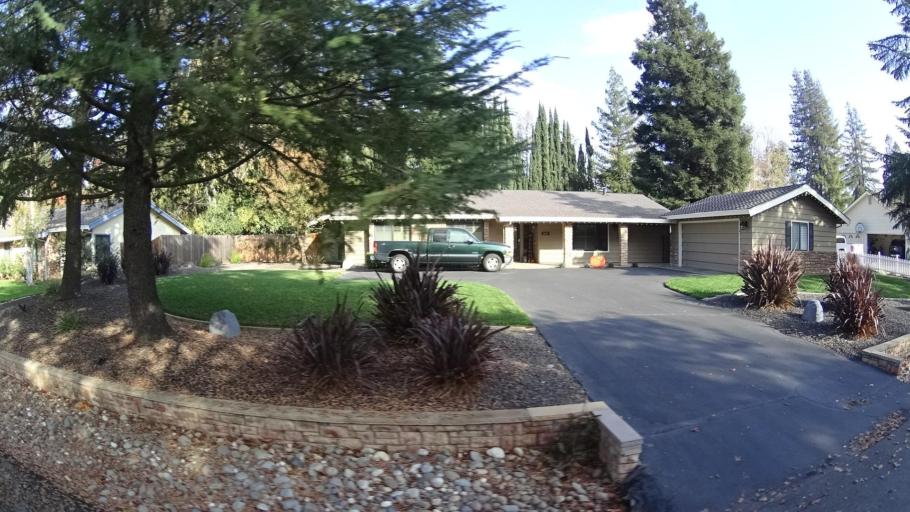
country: US
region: California
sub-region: Sacramento County
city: Elk Grove
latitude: 38.4137
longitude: -121.3650
